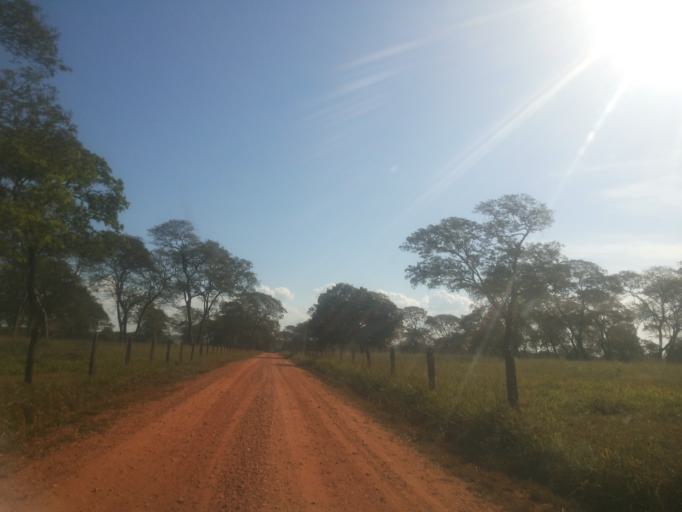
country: BR
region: Minas Gerais
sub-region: Santa Vitoria
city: Santa Vitoria
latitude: -19.0119
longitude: -50.4045
